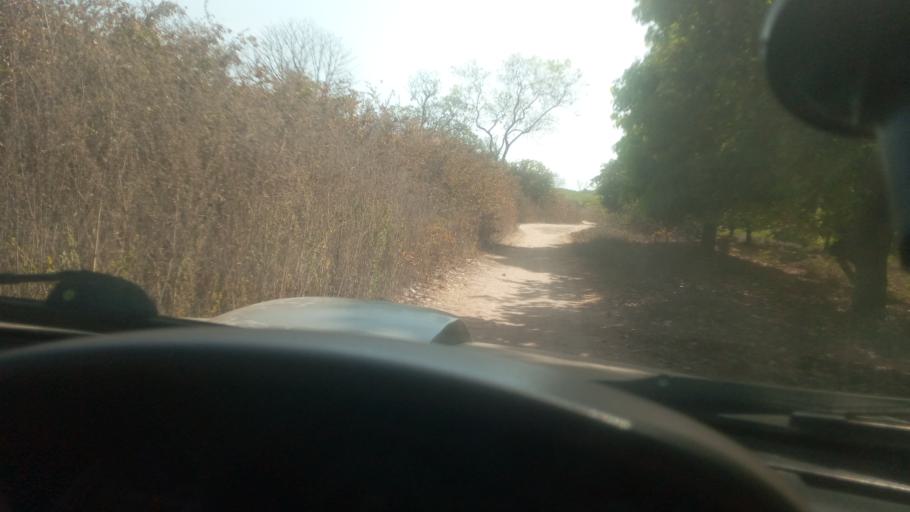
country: GW
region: Oio
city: Farim
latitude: 12.4509
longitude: -15.4258
